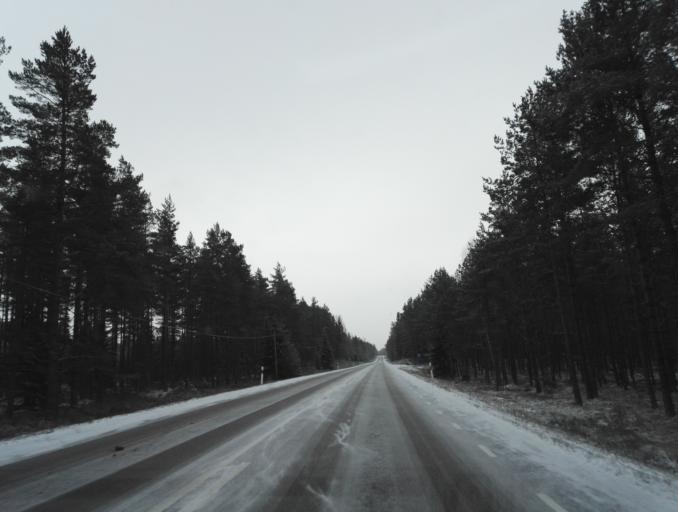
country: SE
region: Kronoberg
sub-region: Uppvidinge Kommun
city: Lenhovda
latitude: 56.9738
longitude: 15.3060
